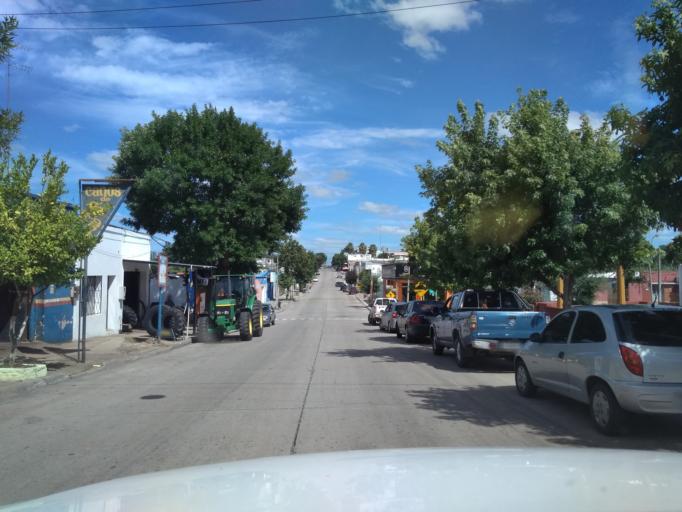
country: UY
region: Florida
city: Florida
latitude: -34.0960
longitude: -56.2107
